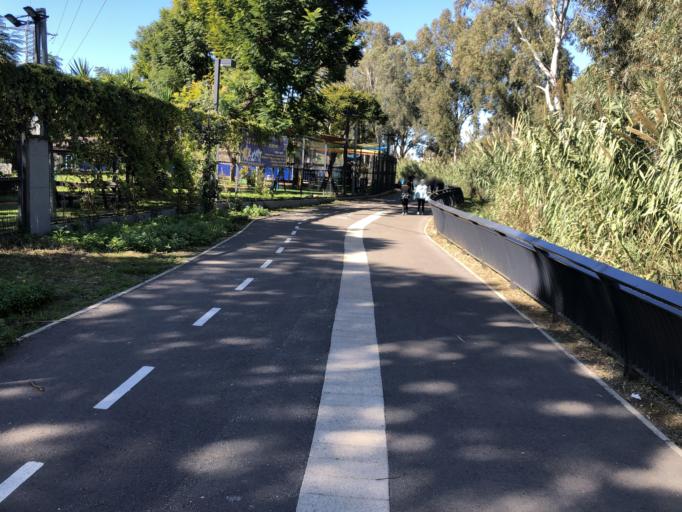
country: IL
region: Tel Aviv
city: Ramat Gan
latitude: 32.0959
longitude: 34.8109
